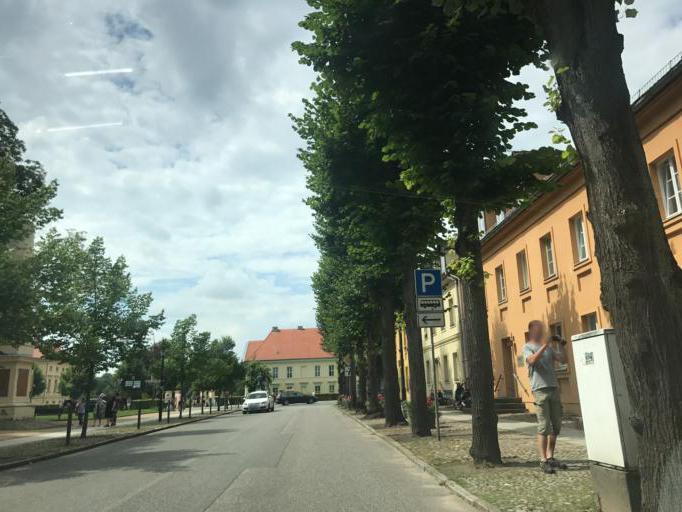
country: DE
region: Brandenburg
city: Rheinsberg
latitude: 53.0990
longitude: 12.8925
